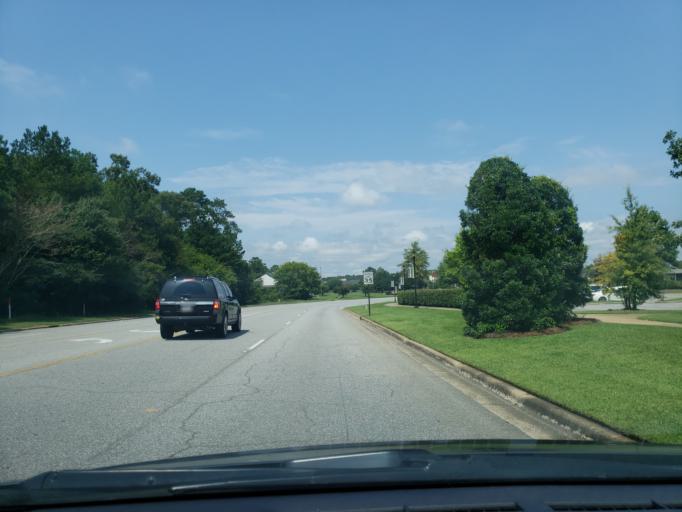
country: US
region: Georgia
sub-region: Dougherty County
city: Albany
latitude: 31.6092
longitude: -84.2172
